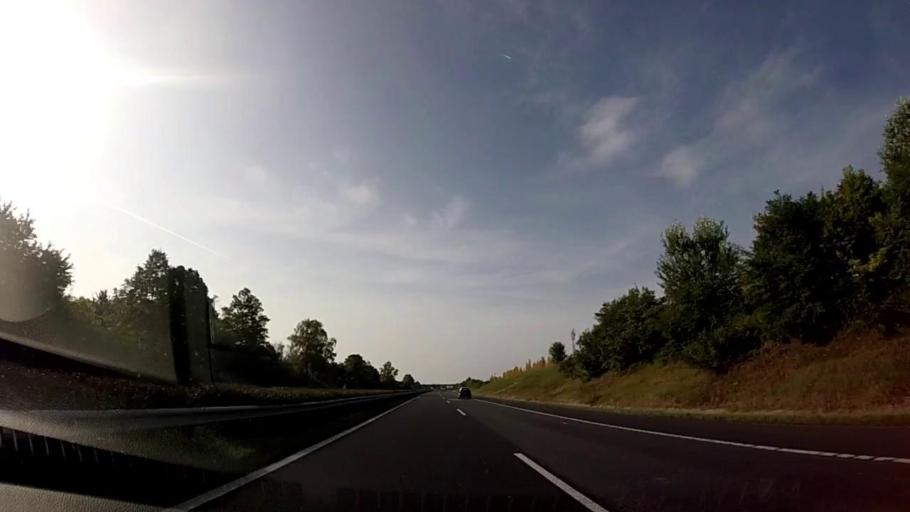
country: HU
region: Fejer
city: Lepseny
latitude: 46.9756
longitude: 18.1721
